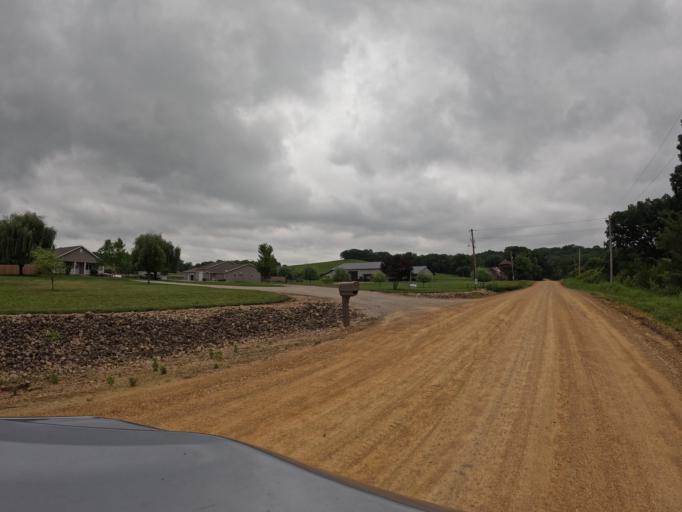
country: US
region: Illinois
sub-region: Carroll County
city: Savanna
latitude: 41.9966
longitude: -90.1813
